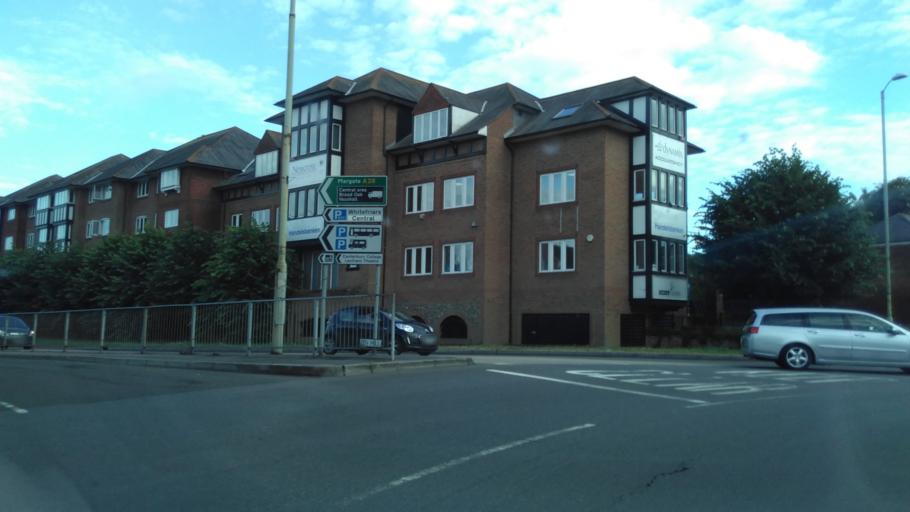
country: GB
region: England
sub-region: Kent
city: Canterbury
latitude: 51.2751
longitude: 1.0747
